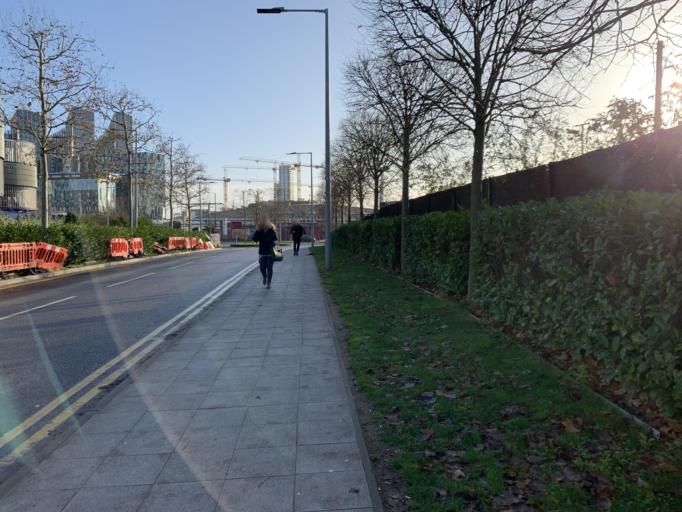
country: GB
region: England
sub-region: Greater London
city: Poplar
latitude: 51.5015
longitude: 0.0013
